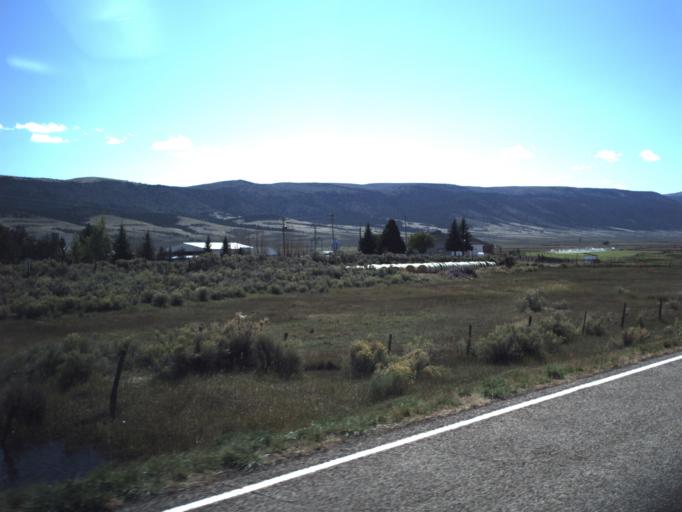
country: US
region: Utah
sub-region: Wayne County
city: Loa
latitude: 38.4933
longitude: -111.8819
